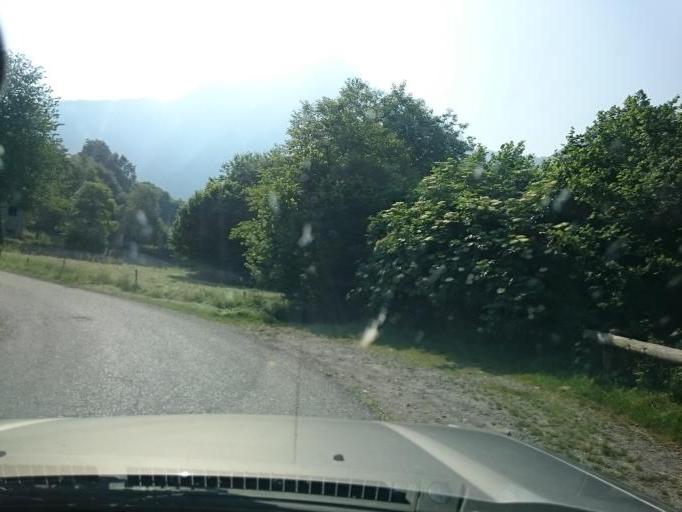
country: IT
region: Lombardy
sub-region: Provincia di Brescia
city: Cimbergo
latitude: 46.0173
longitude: 10.3716
